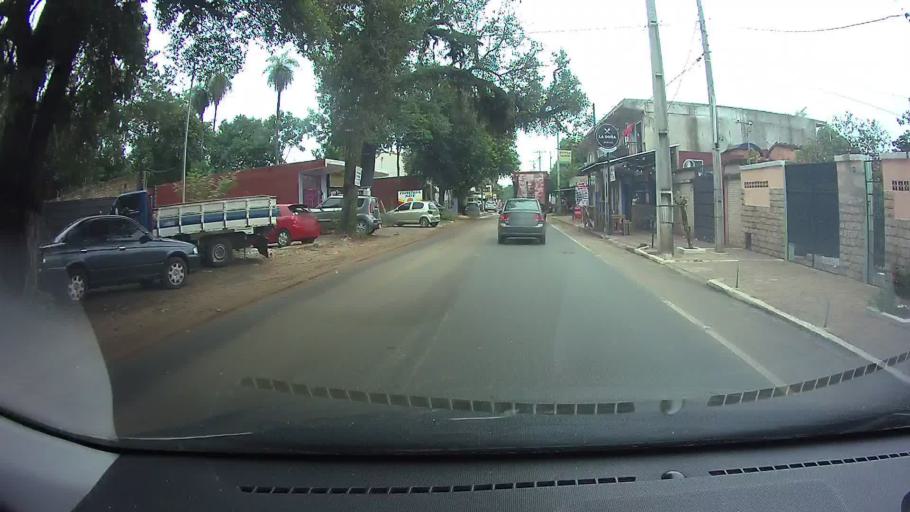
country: PY
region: Central
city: San Lorenzo
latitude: -25.3275
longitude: -57.5044
